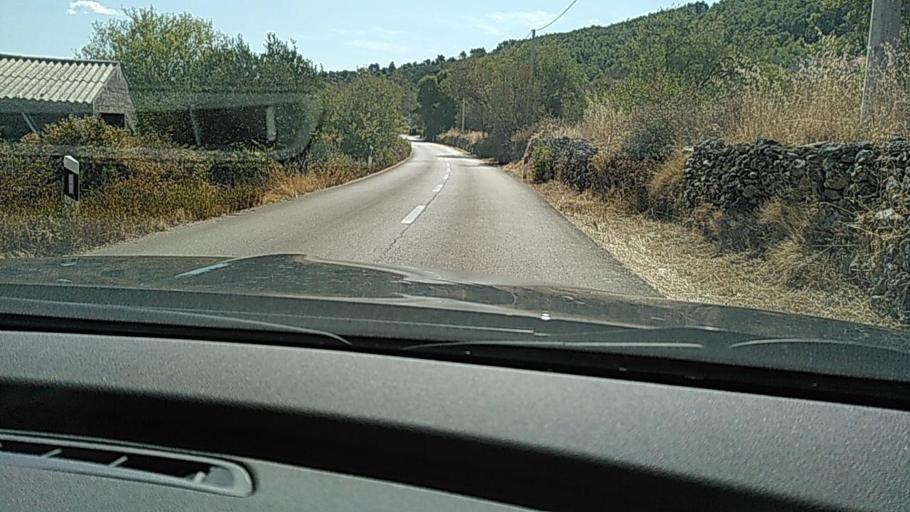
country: HR
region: Splitsko-Dalmatinska
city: Jelsa
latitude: 43.1436
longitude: 16.8436
